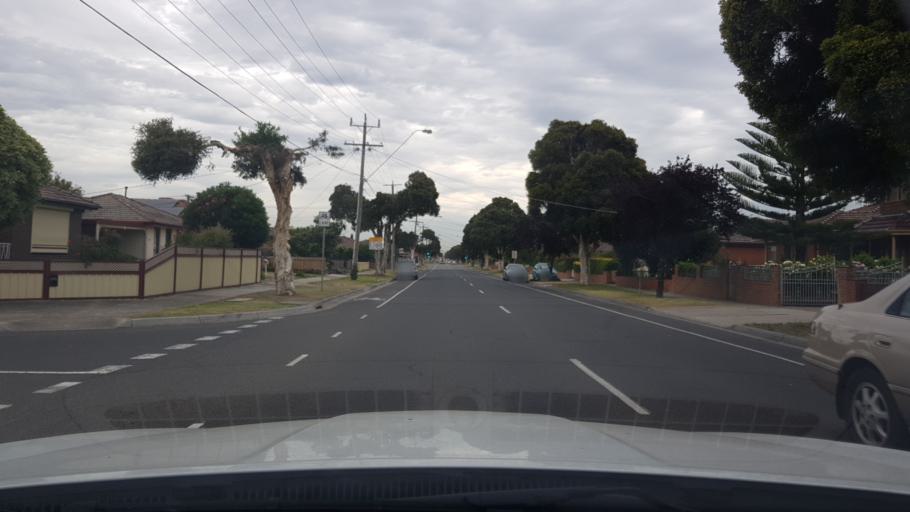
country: AU
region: Victoria
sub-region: Whittlesea
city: Lalor
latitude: -37.6632
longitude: 144.9987
